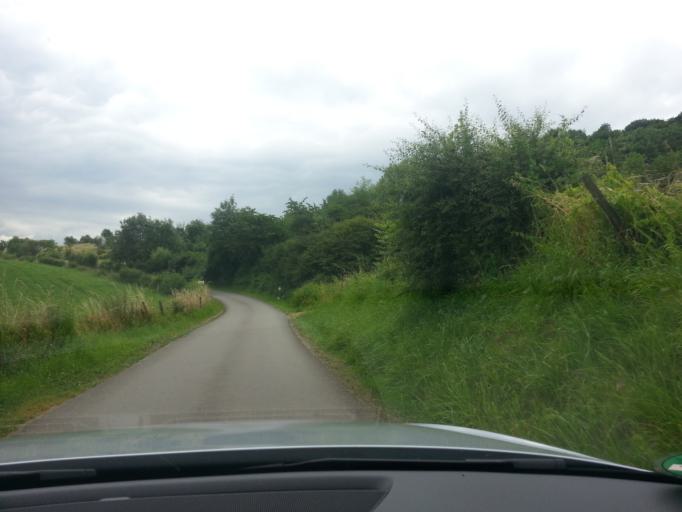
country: LU
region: Grevenmacher
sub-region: Canton de Remich
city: Bous
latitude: 49.5369
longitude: 6.3411
